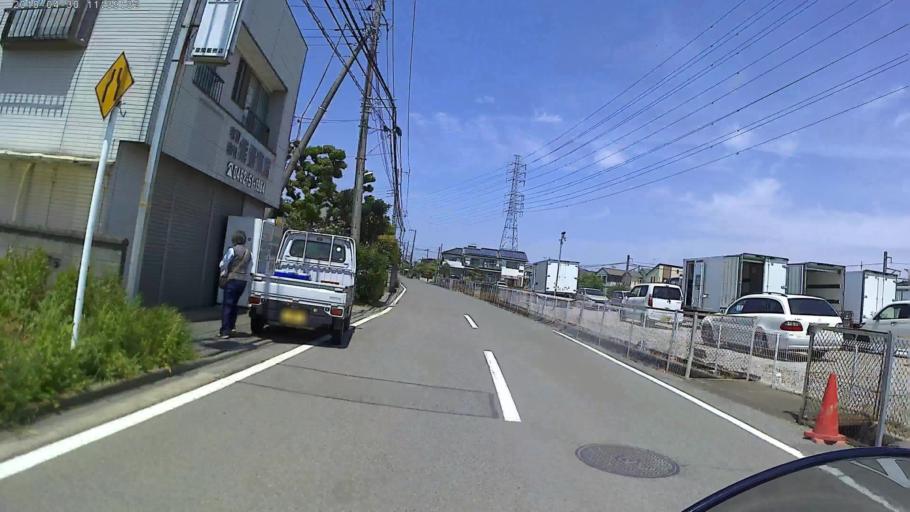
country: JP
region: Kanagawa
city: Zama
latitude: 35.4818
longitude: 139.3894
